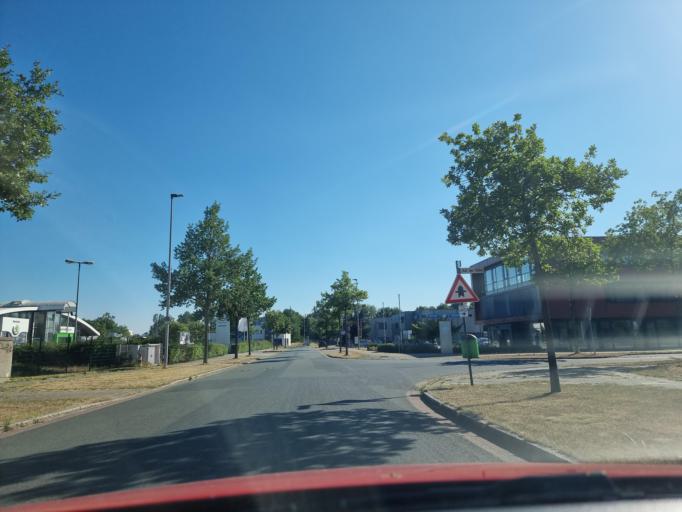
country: DE
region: Lower Saxony
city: Lilienthal
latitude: 53.1076
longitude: 8.8789
